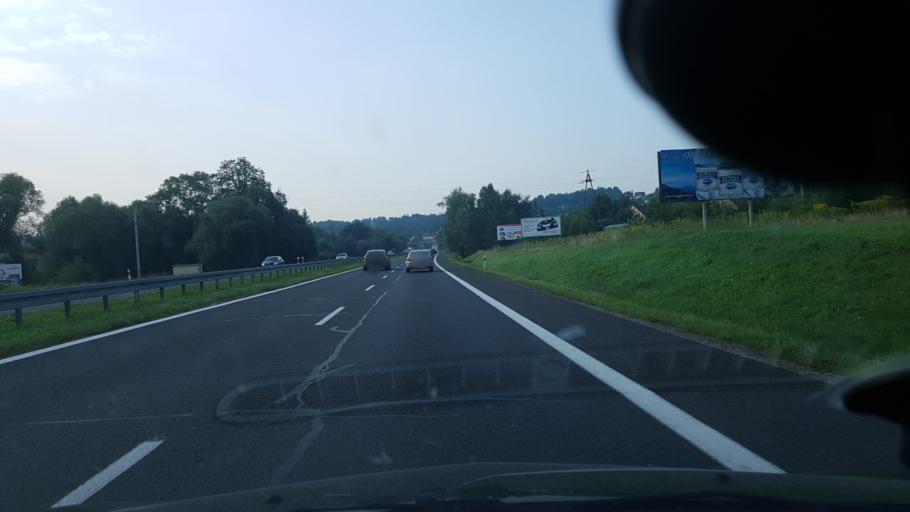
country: PL
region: Lesser Poland Voivodeship
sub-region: Powiat myslenicki
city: Glogoczow
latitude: 49.8983
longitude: 19.8726
